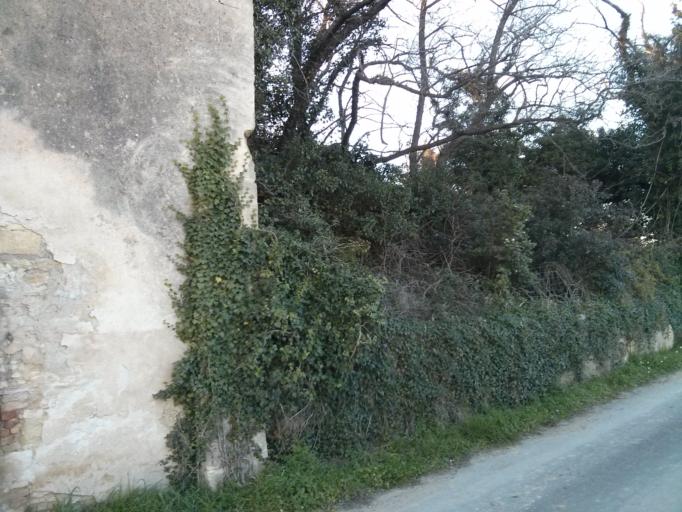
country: FR
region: Languedoc-Roussillon
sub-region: Departement du Gard
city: Aigues-Vives
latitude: 43.7329
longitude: 4.1819
